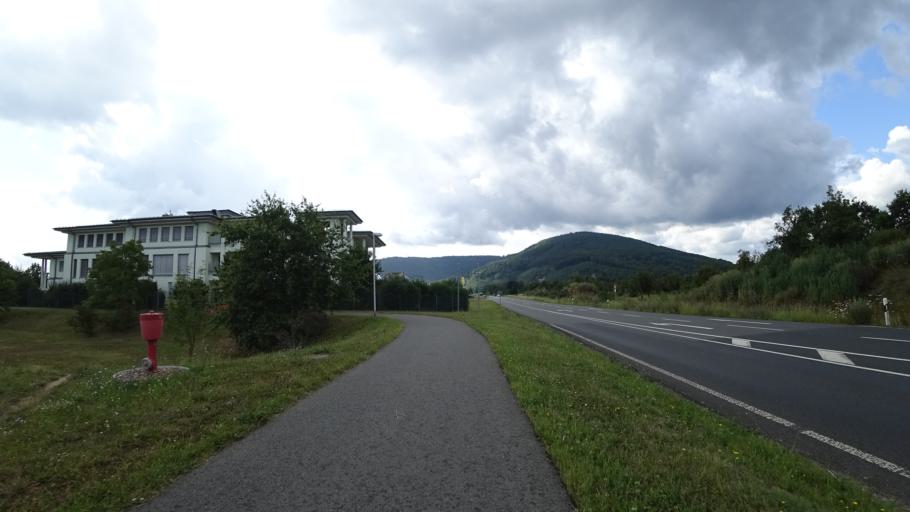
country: DE
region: Bavaria
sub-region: Regierungsbezirk Unterfranken
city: Grossheubach
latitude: 49.7132
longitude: 9.2388
